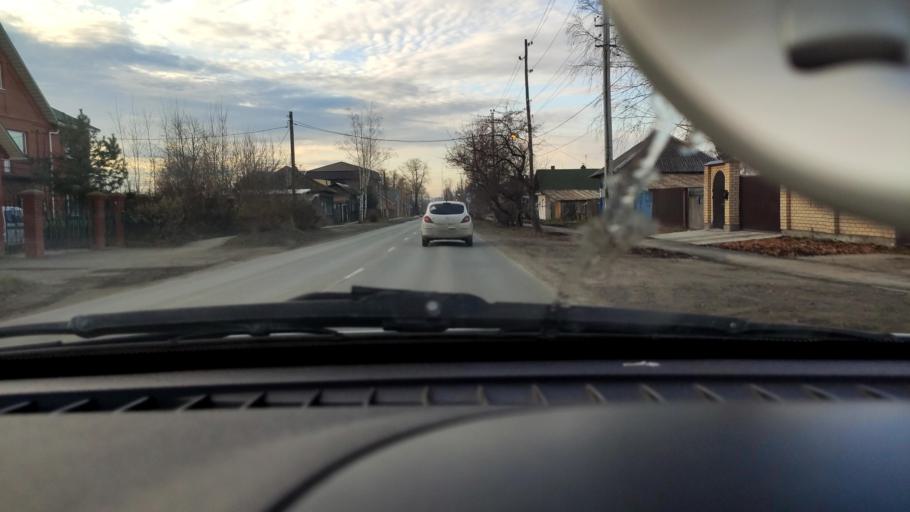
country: RU
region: Perm
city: Perm
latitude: 58.0463
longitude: 56.3304
